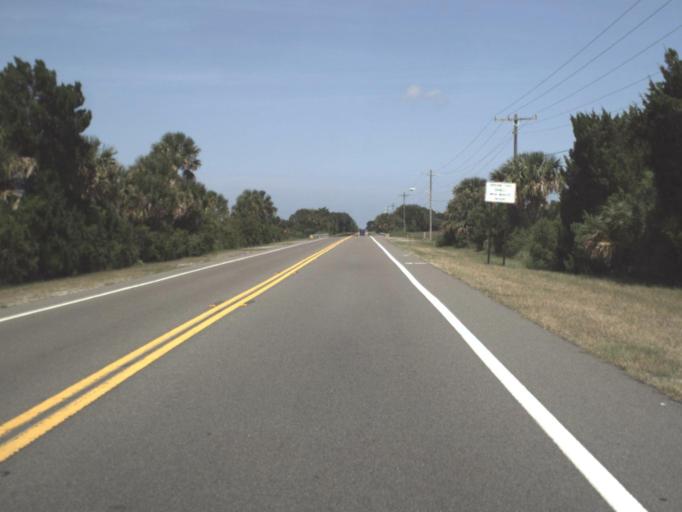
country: US
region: Florida
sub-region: Duval County
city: Atlantic Beach
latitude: 30.3995
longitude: -81.4862
